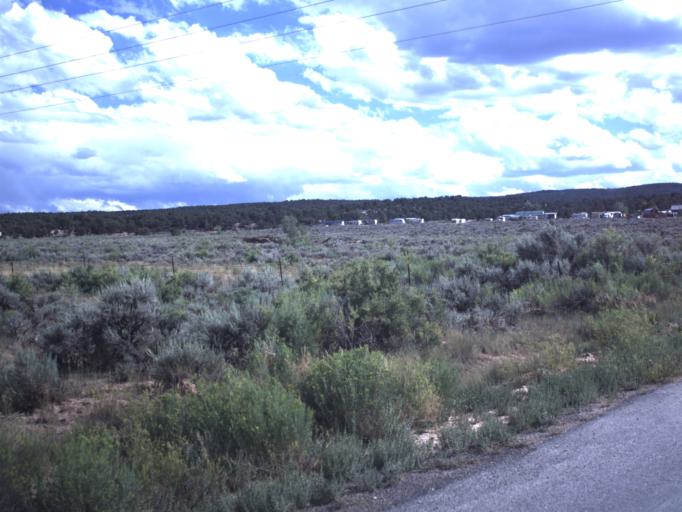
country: US
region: Utah
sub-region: Duchesne County
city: Duchesne
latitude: 40.2059
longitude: -110.7314
